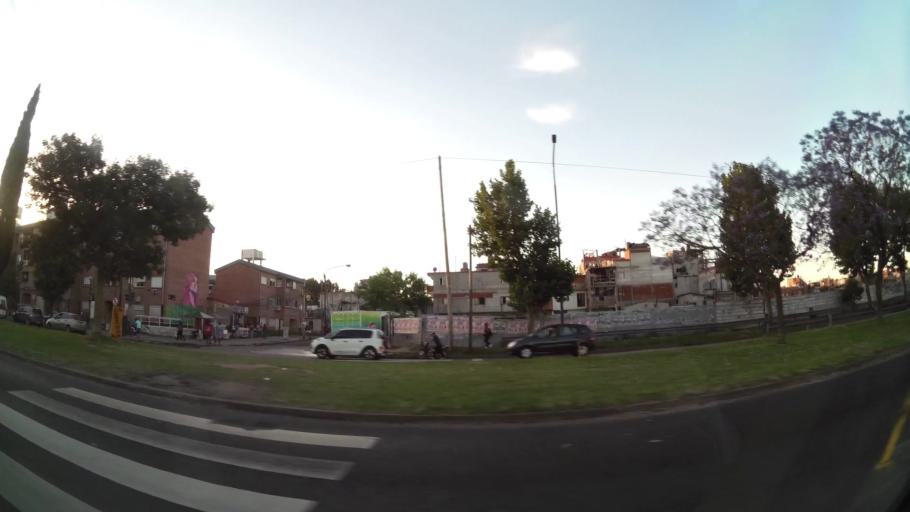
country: AR
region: Buenos Aires F.D.
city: Villa Lugano
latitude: -34.6778
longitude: -58.4644
